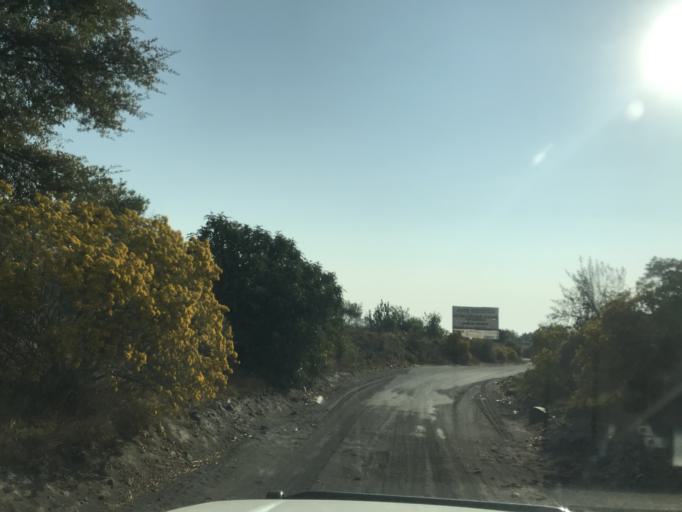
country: MX
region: Puebla
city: San Nicolas de los Ranchos
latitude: 19.0798
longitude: -98.5379
